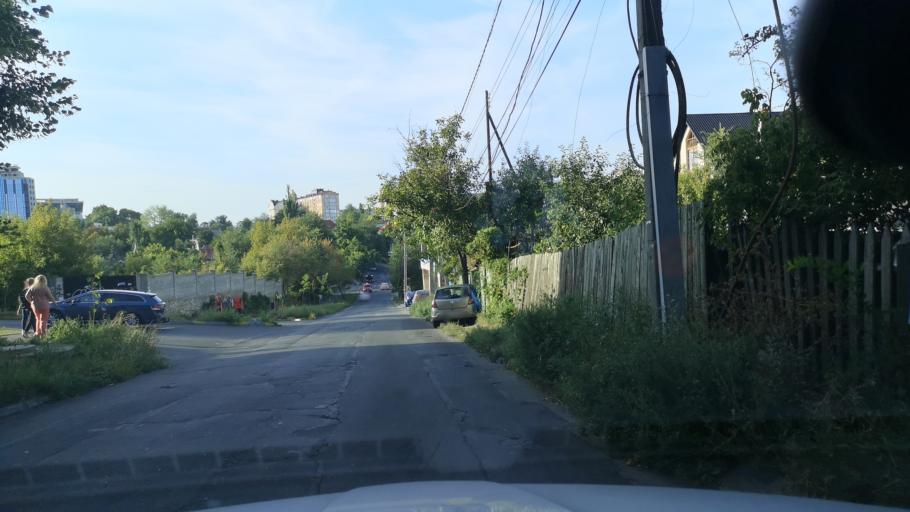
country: MD
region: Chisinau
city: Chisinau
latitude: 47.0090
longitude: 28.8485
